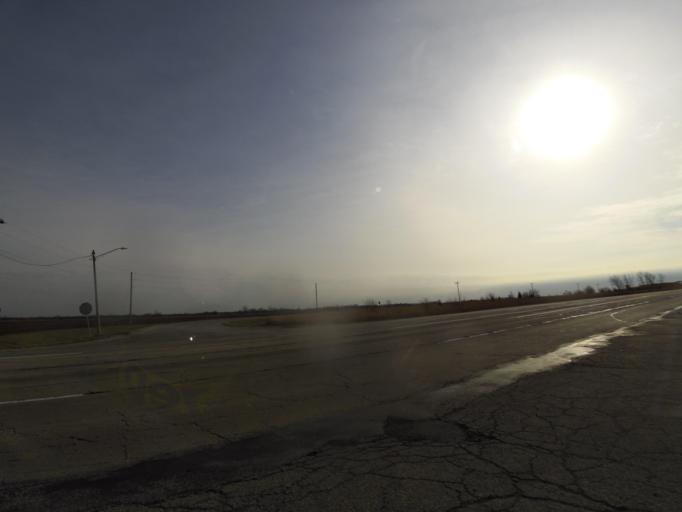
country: US
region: Illinois
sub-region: Macon County
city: Macon
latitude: 39.7707
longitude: -88.9815
